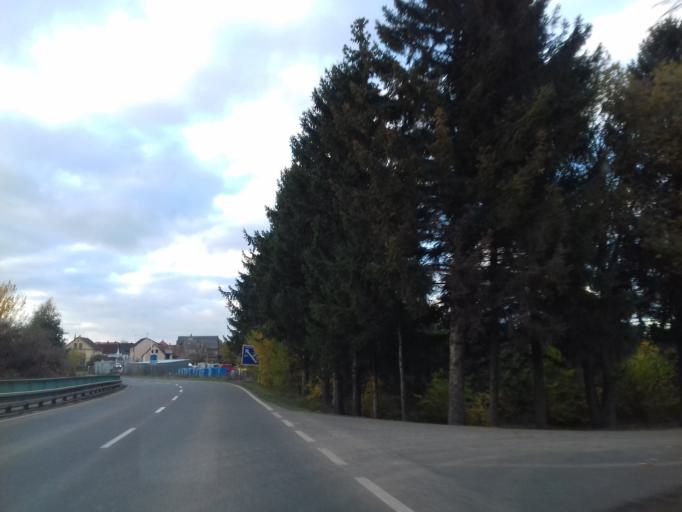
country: CZ
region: Pardubicky
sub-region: Okres Chrudim
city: Skutec
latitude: 49.8397
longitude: 16.0067
